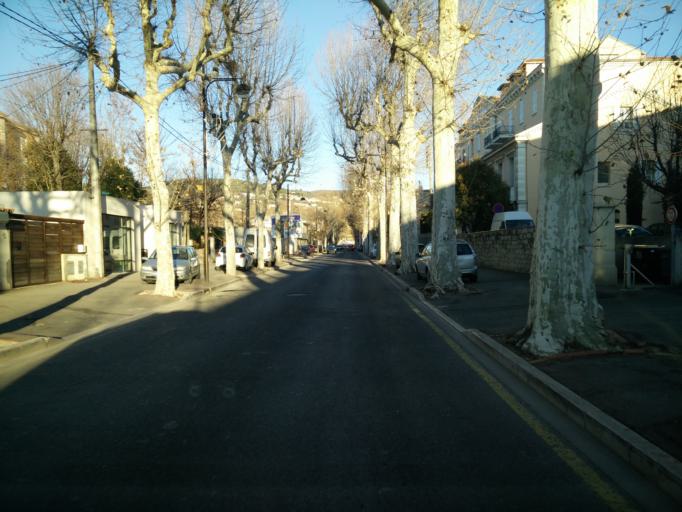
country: FR
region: Provence-Alpes-Cote d'Azur
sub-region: Departement du Var
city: Draguignan
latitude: 43.5353
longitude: 6.4576
